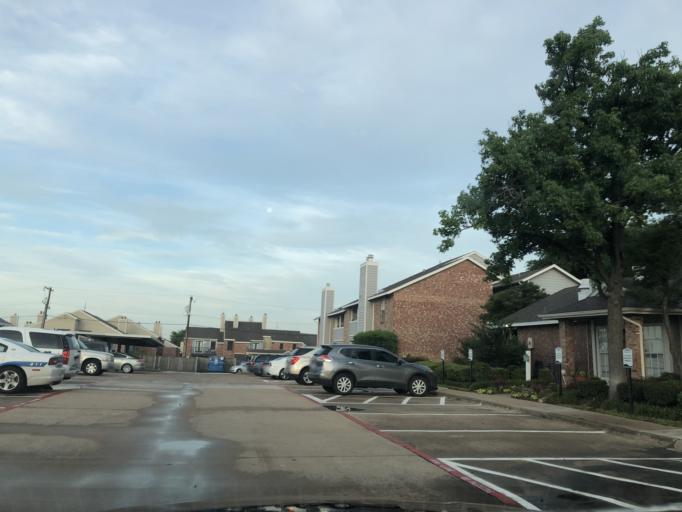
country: US
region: Texas
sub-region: Dallas County
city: Garland
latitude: 32.8424
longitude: -96.6213
